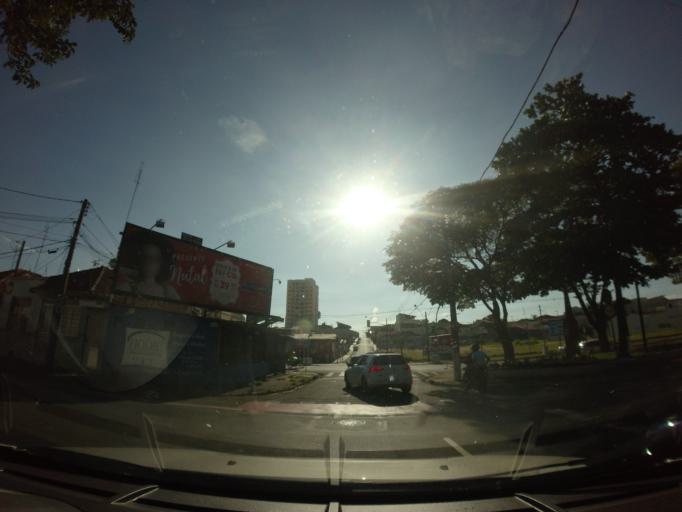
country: BR
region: Sao Paulo
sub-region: Rio Claro
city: Rio Claro
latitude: -22.4047
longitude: -47.5649
